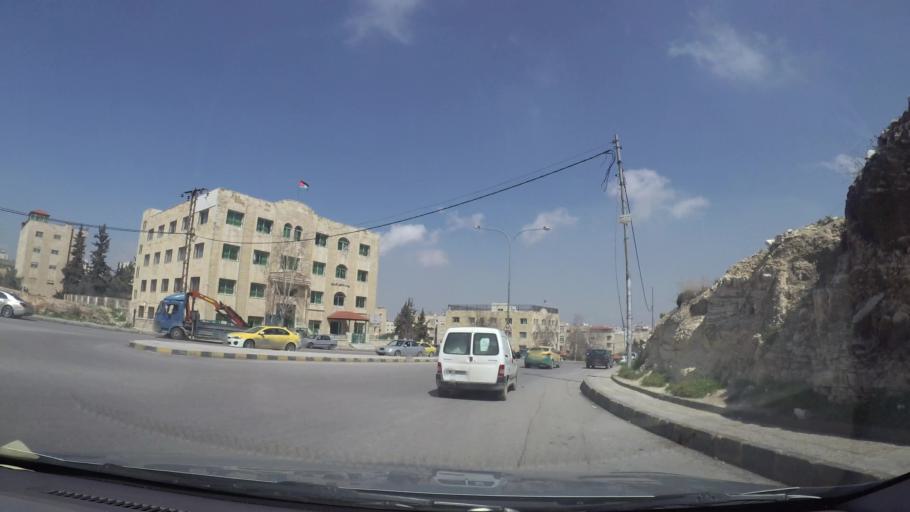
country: JO
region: Amman
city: Al Bunayyat ash Shamaliyah
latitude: 31.9203
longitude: 35.8949
